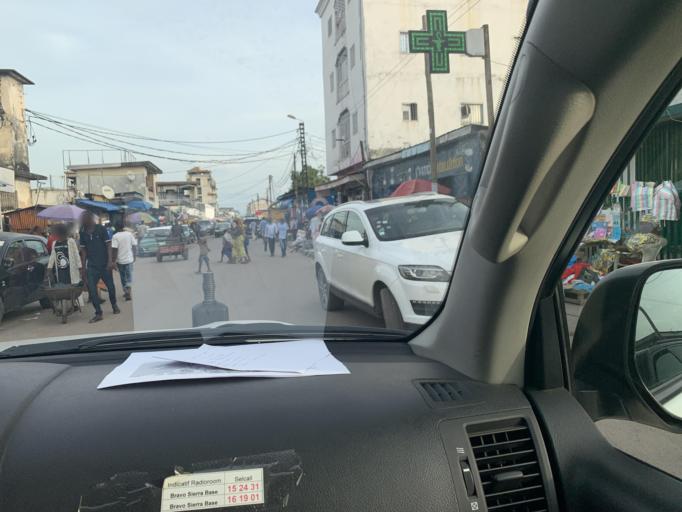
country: CG
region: Brazzaville
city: Brazzaville
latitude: -4.2484
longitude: 15.2837
